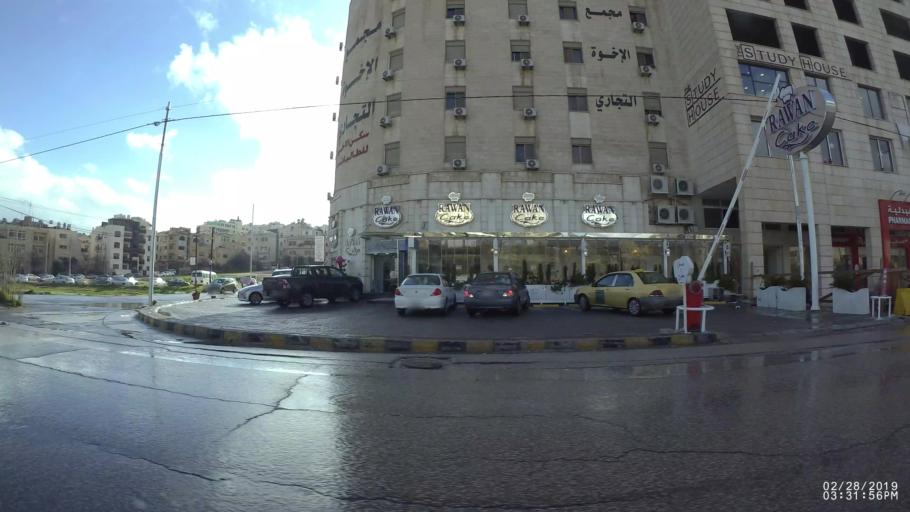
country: JO
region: Amman
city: Al Jubayhah
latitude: 32.0066
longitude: 35.8724
